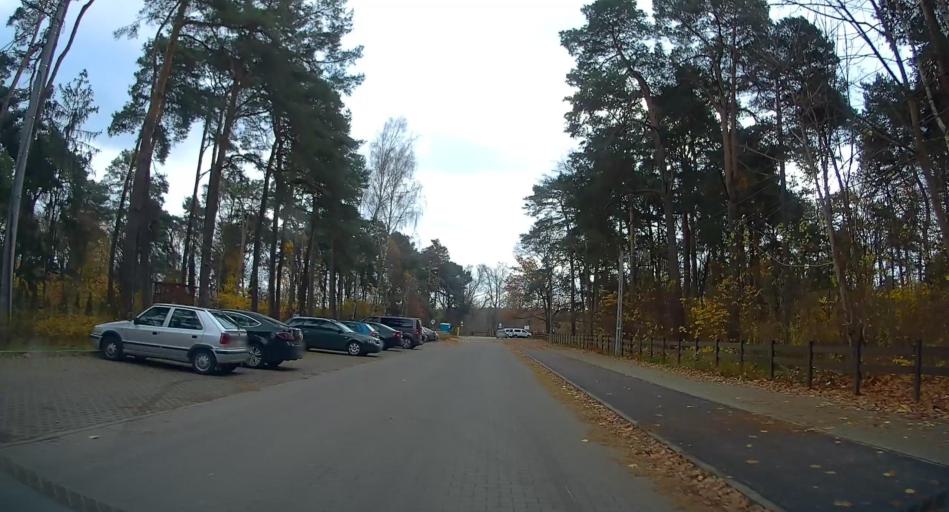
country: PL
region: Masovian Voivodeship
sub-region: Powiat piaseczynski
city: Zabieniec
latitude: 52.0526
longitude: 21.0235
